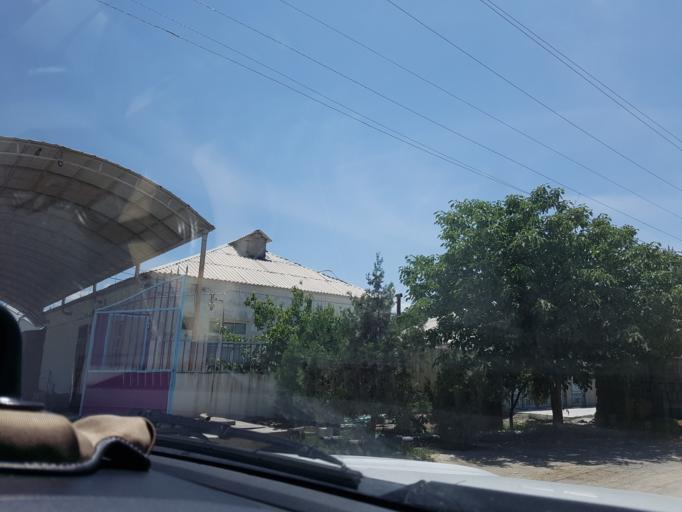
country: TM
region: Ahal
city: Abadan
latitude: 38.1746
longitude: 57.9558
